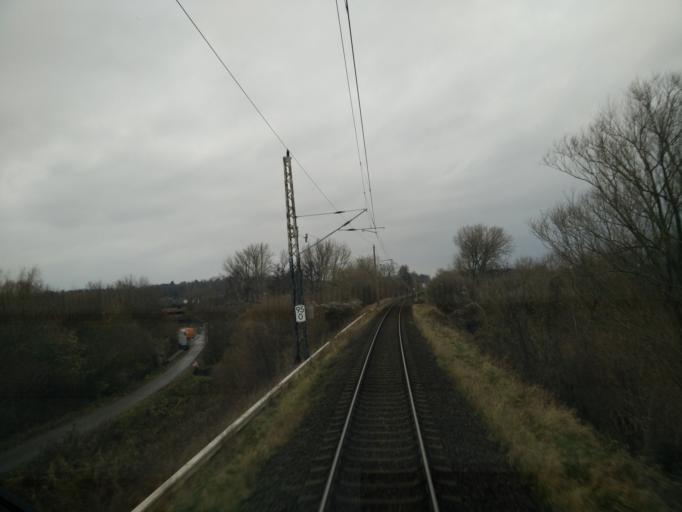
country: DE
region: Mecklenburg-Vorpommern
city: Mecklenburg
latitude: 53.8684
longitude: 11.4657
